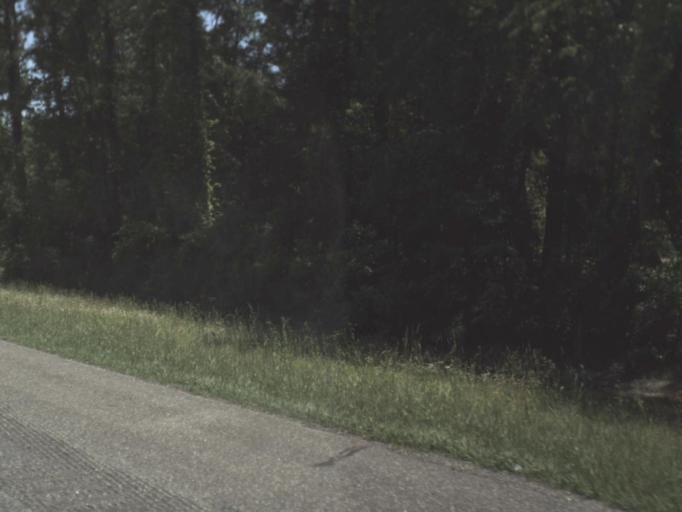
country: US
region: Florida
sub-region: Jefferson County
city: Monticello
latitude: 30.4887
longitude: -83.9796
